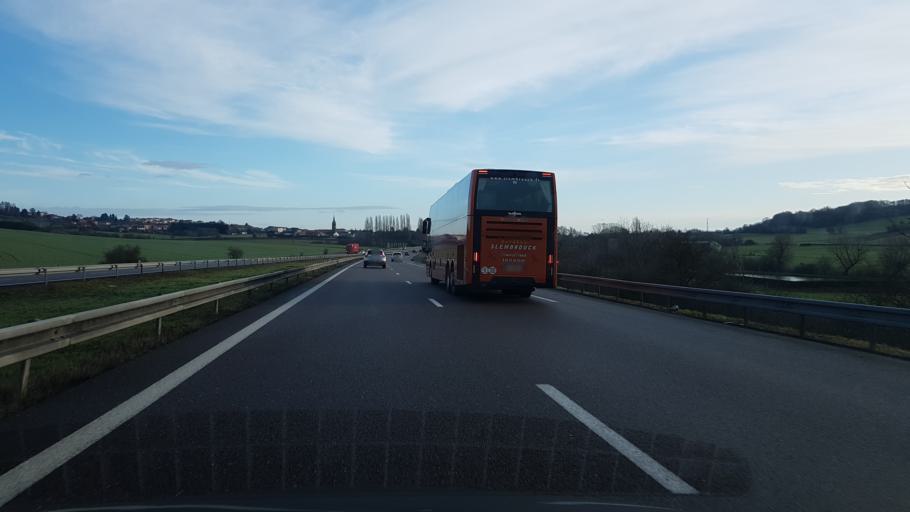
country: FR
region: Lorraine
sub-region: Departement de la Moselle
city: Longeville-les-Saint-Avold
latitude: 49.1362
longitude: 6.5924
